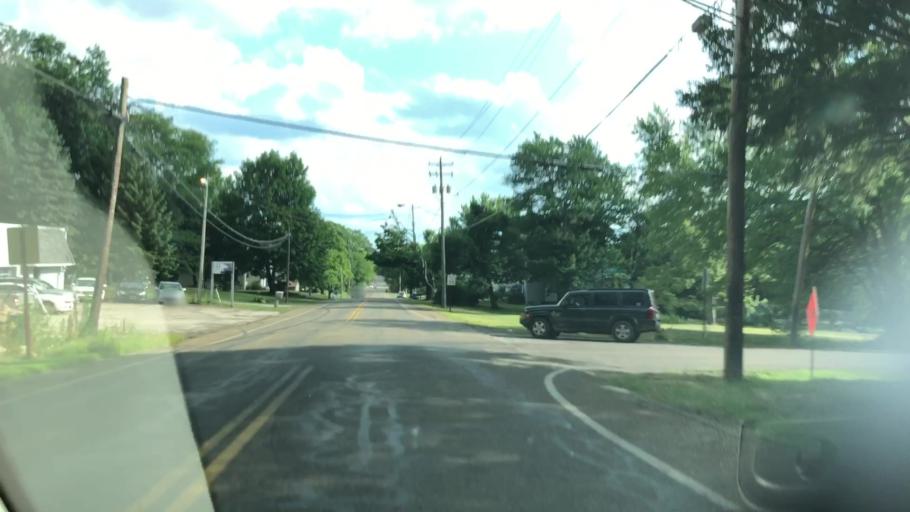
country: US
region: Ohio
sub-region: Summit County
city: Norton
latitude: 41.0550
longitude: -81.6375
